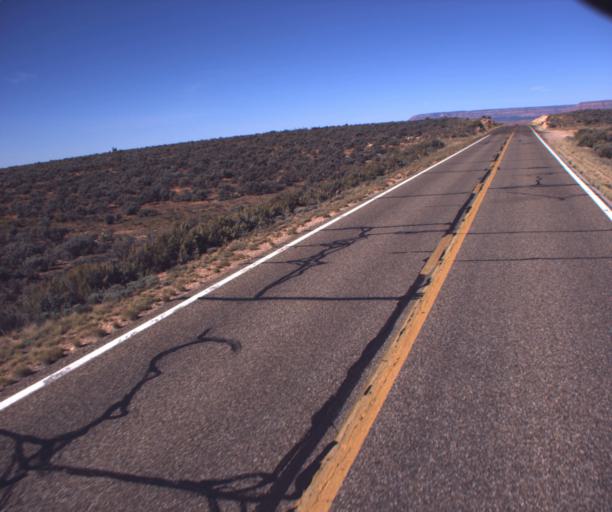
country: US
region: Arizona
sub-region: Coconino County
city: Fredonia
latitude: 36.8947
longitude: -112.3630
